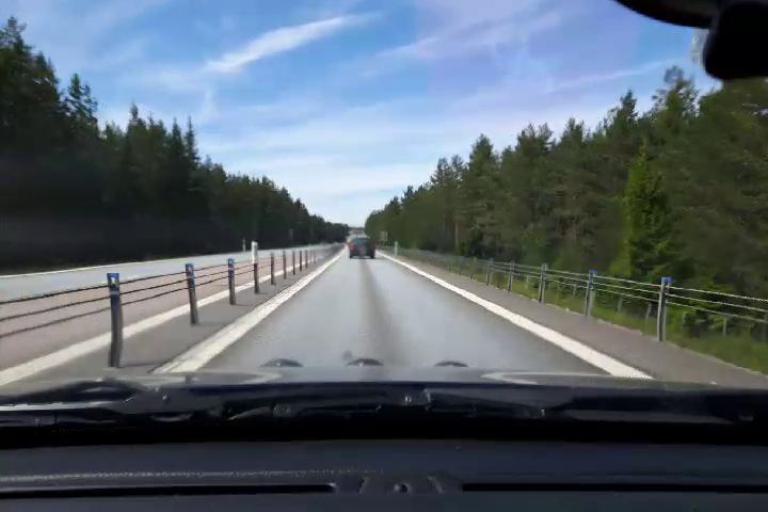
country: SE
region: Gaevleborg
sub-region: Gavle Kommun
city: Norrsundet
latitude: 60.8525
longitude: 17.0694
